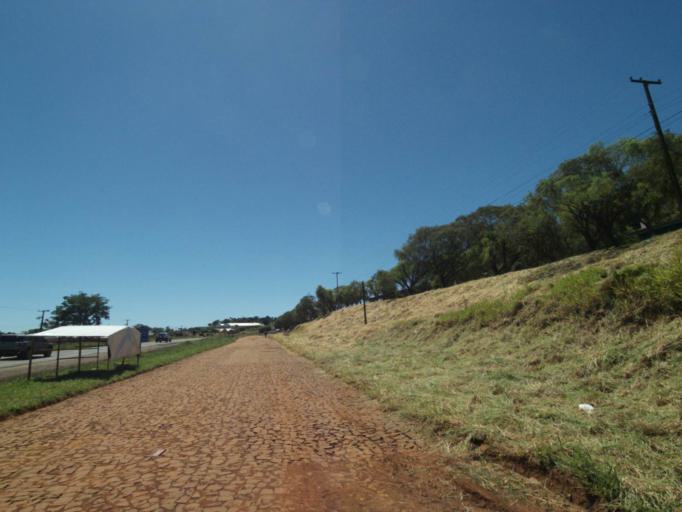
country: BR
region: Parana
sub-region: Pato Branco
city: Pato Branco
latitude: -26.2593
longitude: -52.7718
